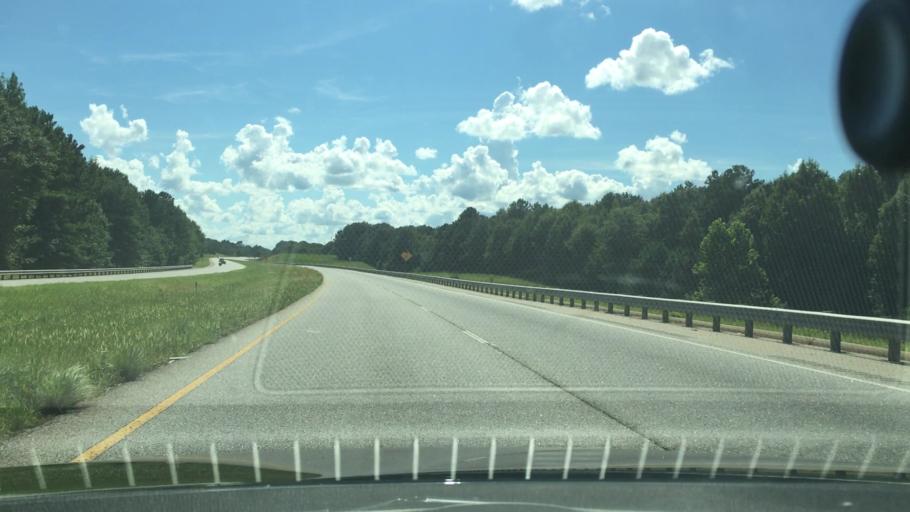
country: US
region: Georgia
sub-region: Spalding County
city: East Griffin
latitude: 33.2377
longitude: -84.2117
